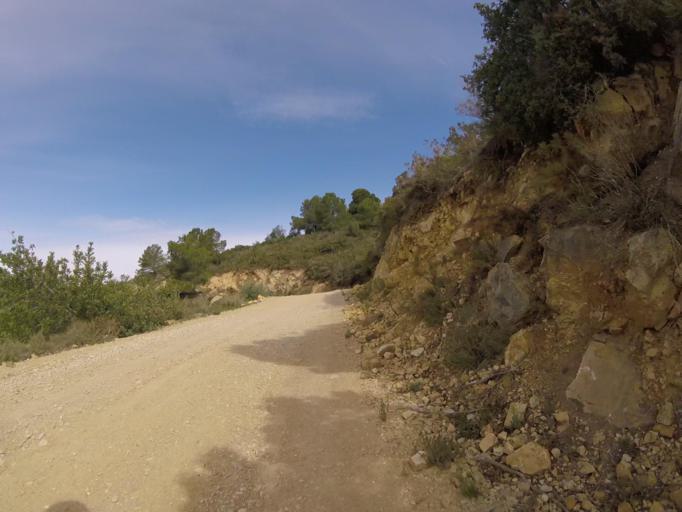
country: ES
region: Valencia
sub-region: Provincia de Castello
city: Torreblanca
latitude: 40.2046
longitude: 0.1504
